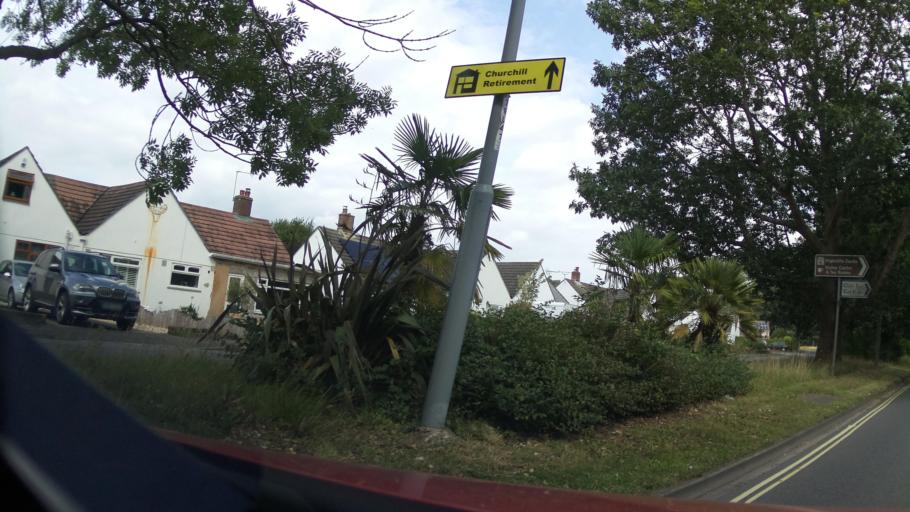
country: GB
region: England
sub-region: Hampshire
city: Bransgore
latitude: 50.7399
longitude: -1.7138
